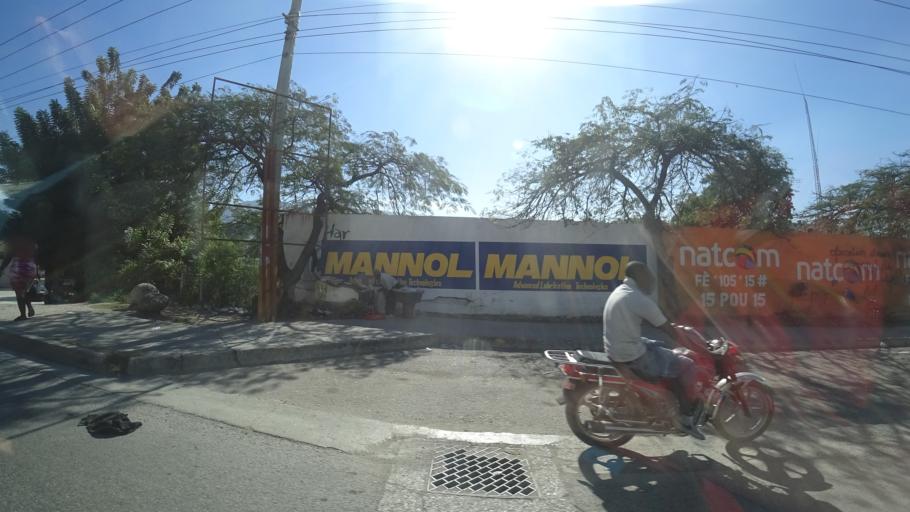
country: HT
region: Ouest
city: Delmas 73
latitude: 18.5580
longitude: -72.3182
